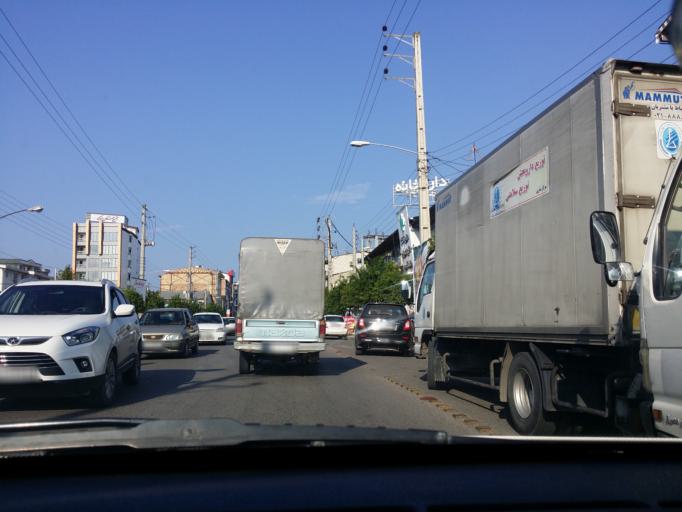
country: IR
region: Mazandaran
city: Chalus
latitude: 36.6562
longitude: 51.4184
